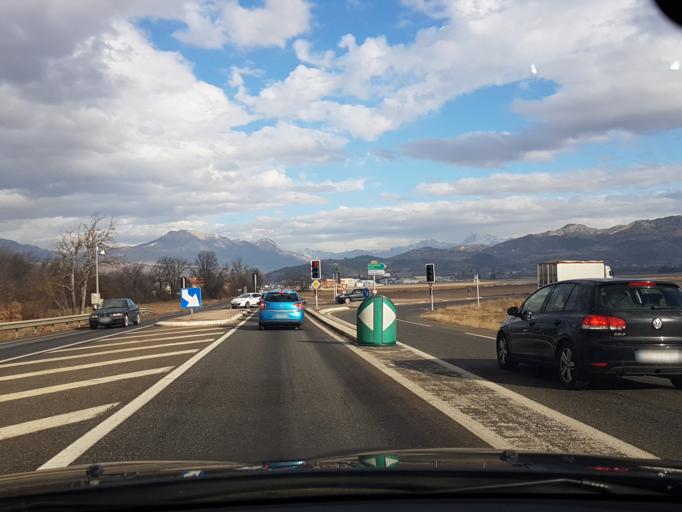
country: FR
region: Provence-Alpes-Cote d'Azur
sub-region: Departement des Hautes-Alpes
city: Tallard
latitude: 44.4470
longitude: 6.0323
